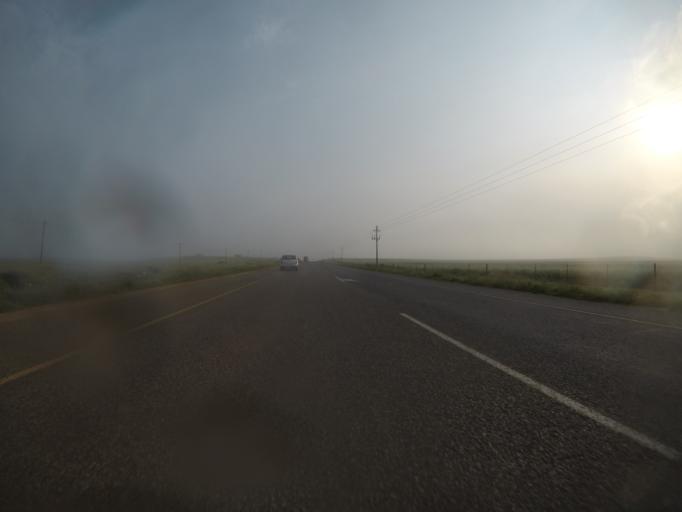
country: ZA
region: Western Cape
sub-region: City of Cape Town
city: Kraaifontein
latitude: -33.6648
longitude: 18.7077
